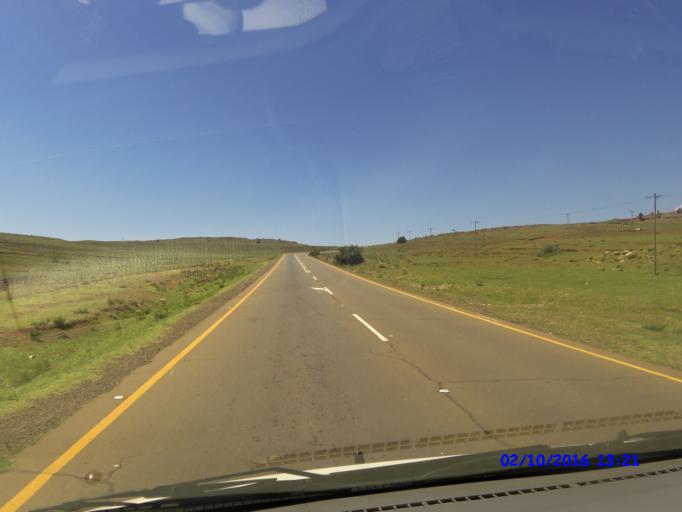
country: LS
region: Maseru
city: Nako
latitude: -29.4216
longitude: 27.7091
